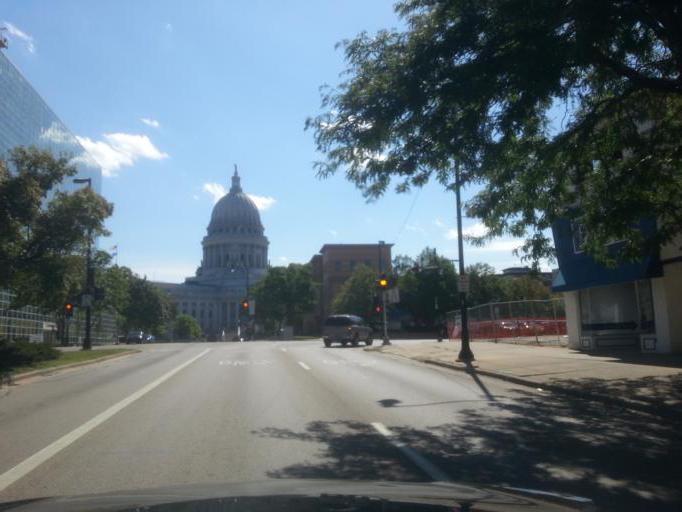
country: US
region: Wisconsin
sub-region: Dane County
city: Madison
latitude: 43.0765
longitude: -89.3818
